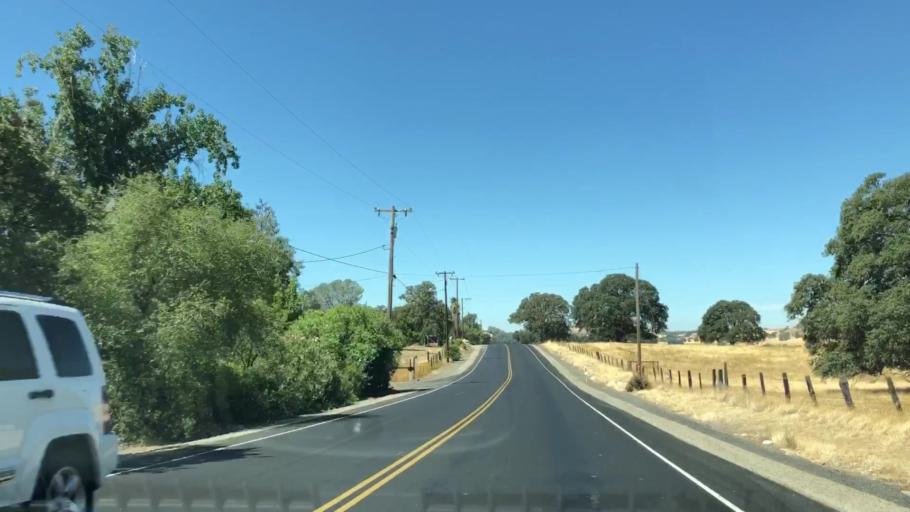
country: US
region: California
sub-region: Tuolumne County
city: Jamestown
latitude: 37.8761
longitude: -120.4389
